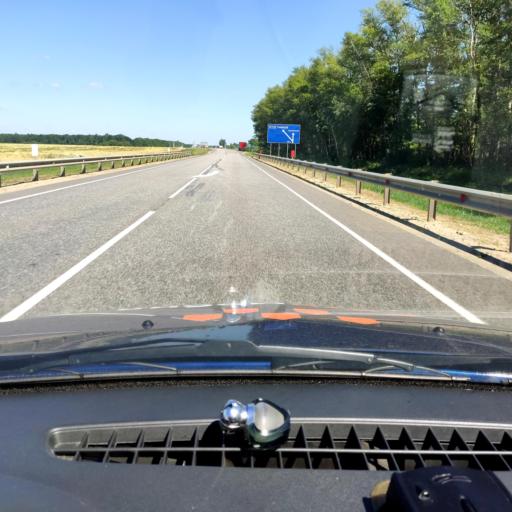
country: RU
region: Orjol
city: Pokrovskoye
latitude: 52.6203
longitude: 36.7609
